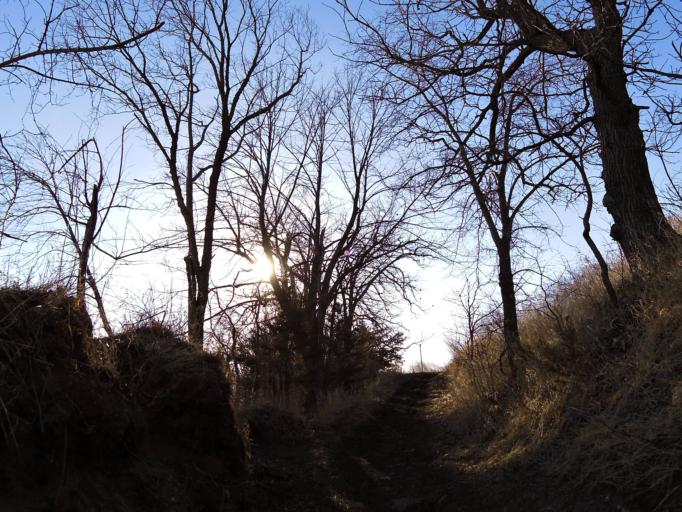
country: US
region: Minnesota
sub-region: Scott County
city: Prior Lake
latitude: 44.7061
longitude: -93.4719
